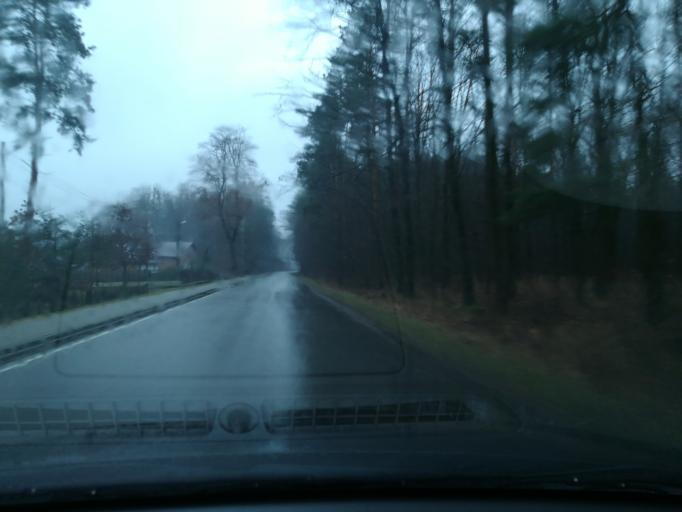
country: PL
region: Subcarpathian Voivodeship
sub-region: Powiat lancucki
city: Bialobrzegi
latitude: 50.1190
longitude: 22.3511
